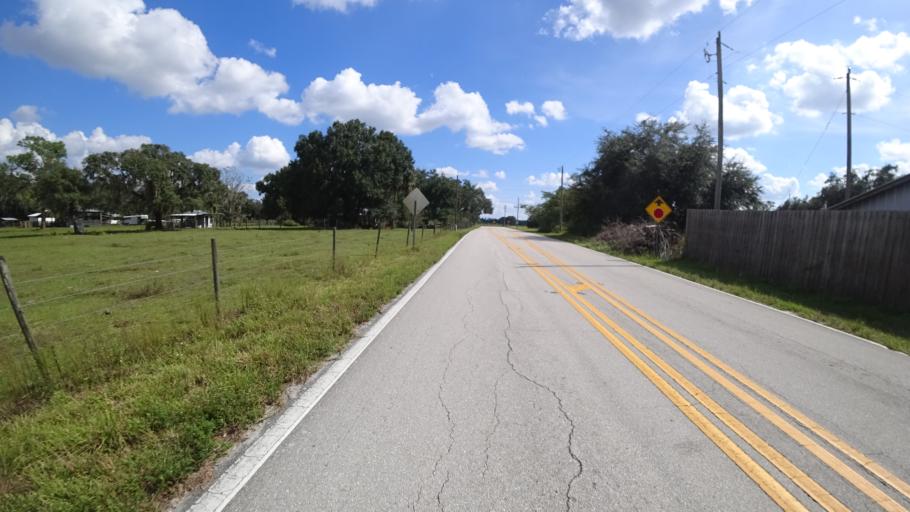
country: US
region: Florida
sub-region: Hardee County
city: Wauchula
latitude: 27.4694
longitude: -82.0767
